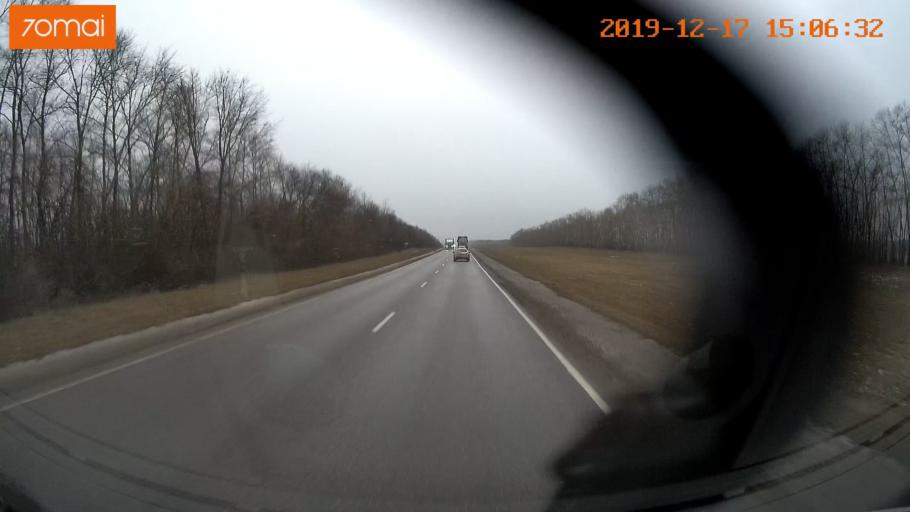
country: RU
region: Rjazan
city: Mikhaylov
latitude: 54.2584
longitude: 39.0982
